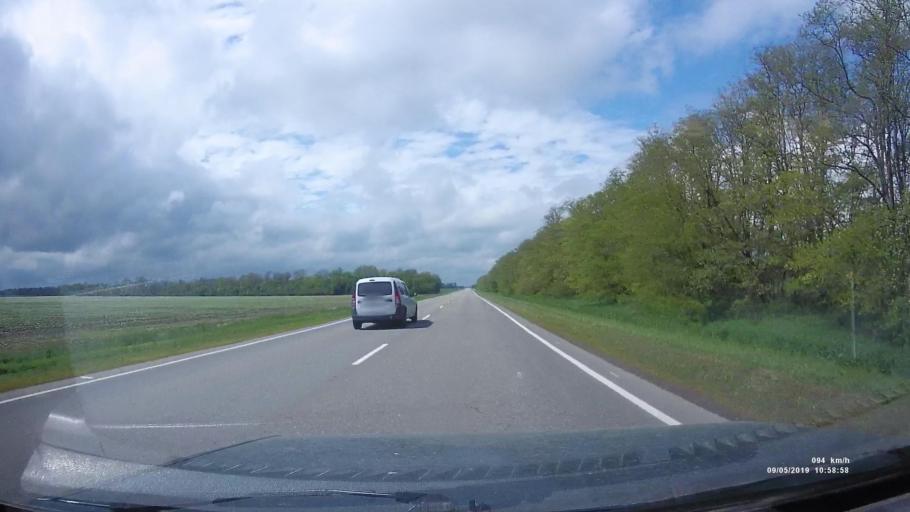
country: RU
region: Rostov
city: Peshkovo
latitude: 46.8592
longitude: 39.2489
